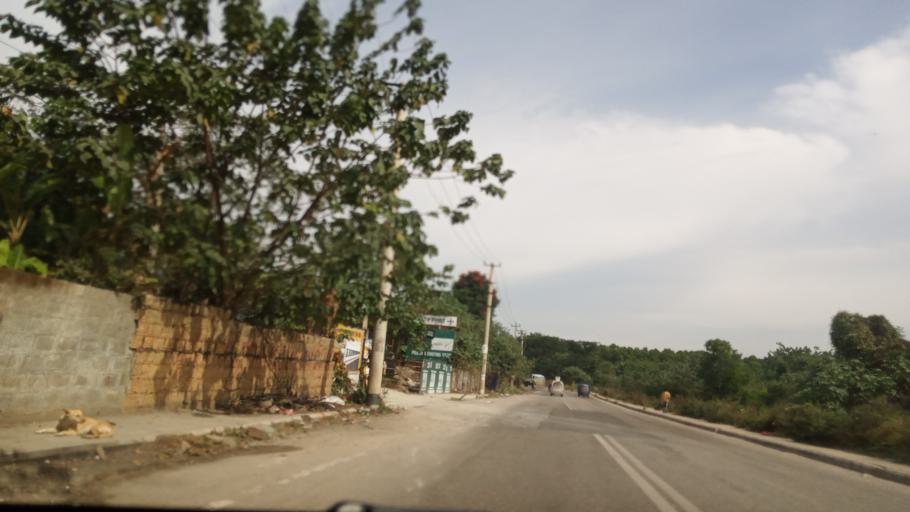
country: IN
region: Karnataka
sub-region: Bangalore Urban
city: Yelahanka
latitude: 13.0411
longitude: 77.5390
